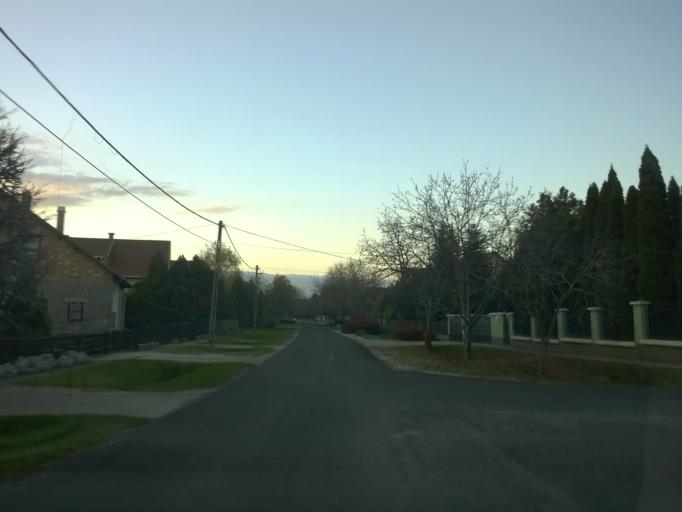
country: HU
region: Pest
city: Szigetcsep
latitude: 47.2689
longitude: 18.9677
